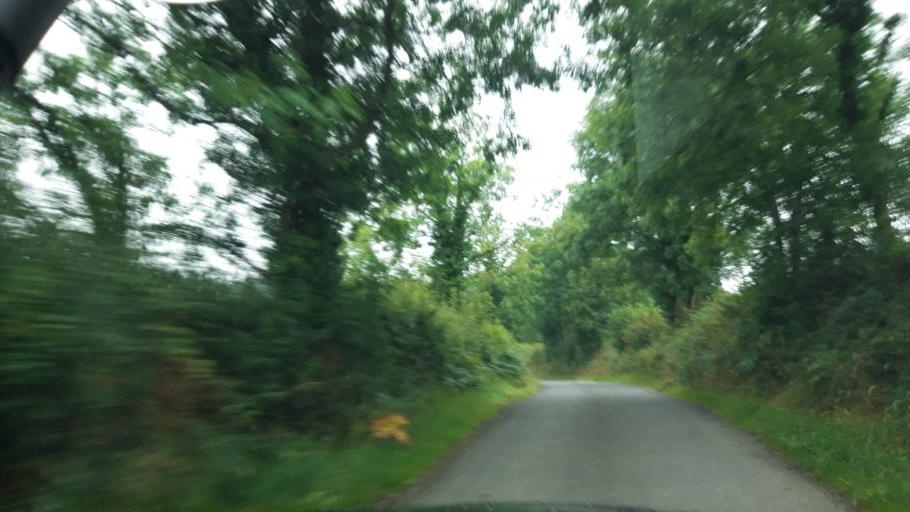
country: IE
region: Leinster
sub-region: Kilkenny
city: Callan
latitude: 52.6388
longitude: -7.5094
